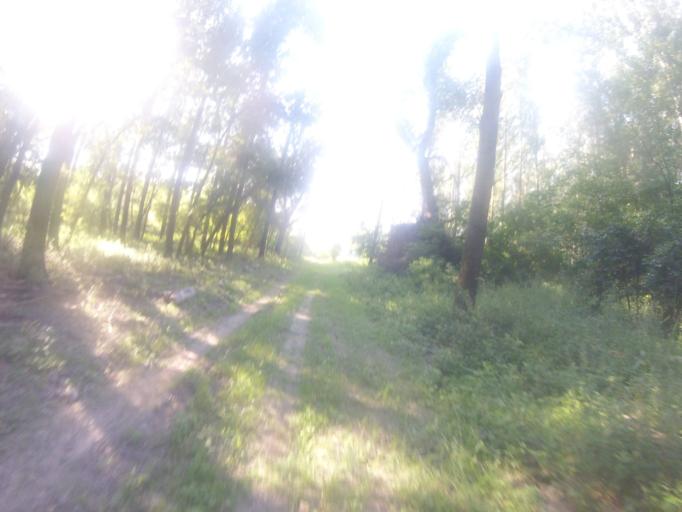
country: HU
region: Bacs-Kiskun
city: Baja
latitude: 46.1822
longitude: 18.9186
